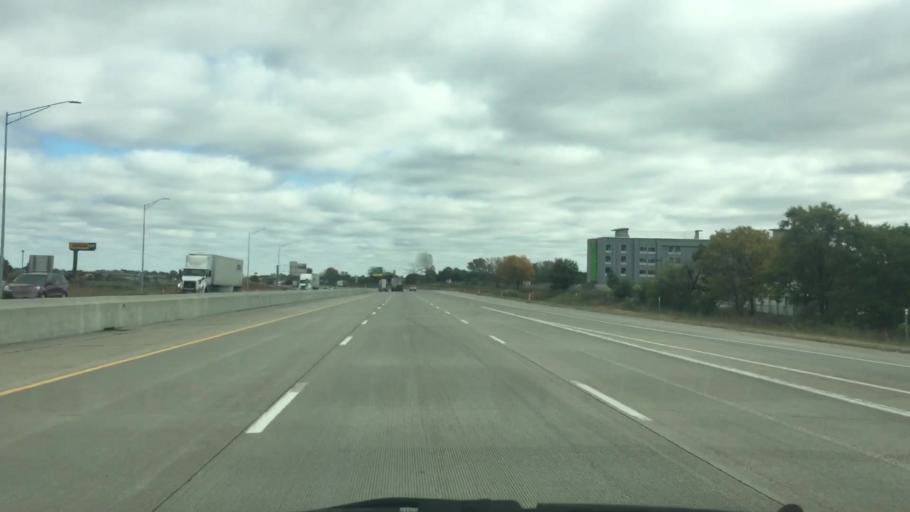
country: US
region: Iowa
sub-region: Polk County
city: Altoona
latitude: 41.6619
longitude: -93.4878
